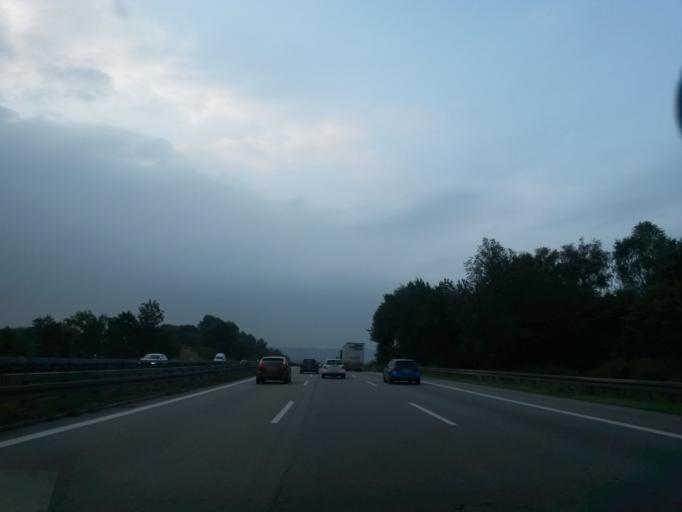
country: DE
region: Bavaria
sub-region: Upper Bavaria
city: Rohrbach
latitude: 48.6058
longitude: 11.5482
